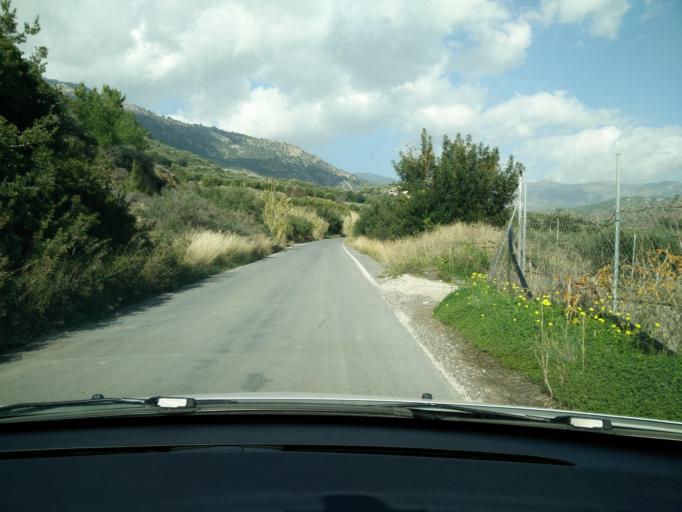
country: GR
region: Crete
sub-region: Nomos Lasithiou
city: Gra Liyia
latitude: 35.0252
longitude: 25.5807
